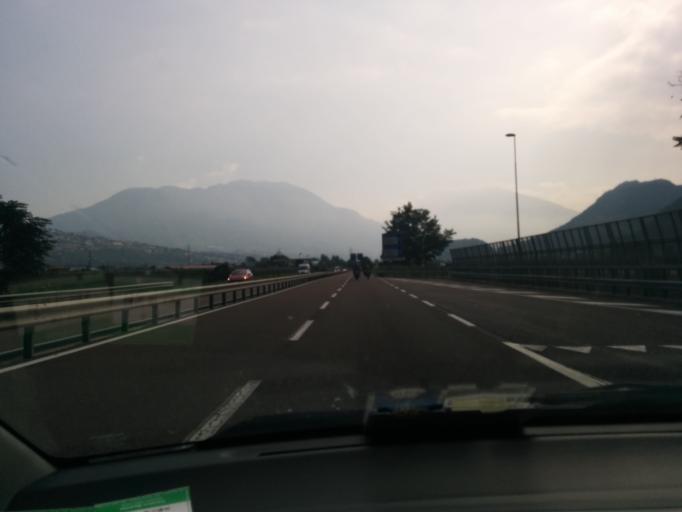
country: IT
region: Trentino-Alto Adige
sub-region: Provincia di Trento
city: Cadine
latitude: 46.0979
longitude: 11.0951
